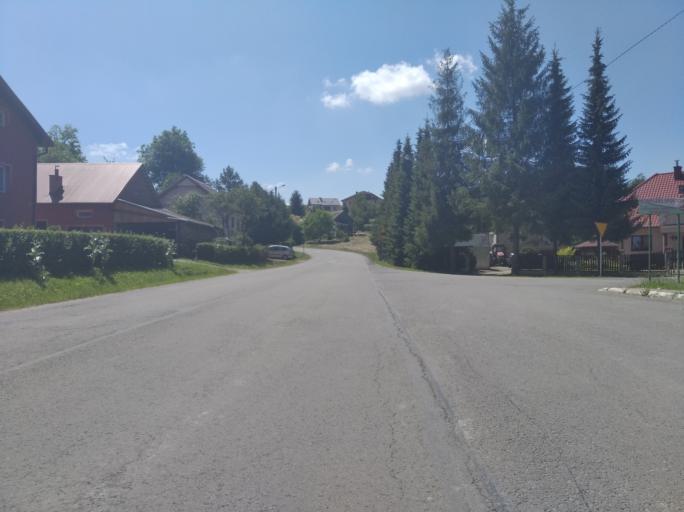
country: PL
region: Subcarpathian Voivodeship
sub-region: Powiat brzozowski
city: Jablonka
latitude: 49.6936
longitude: 22.1151
